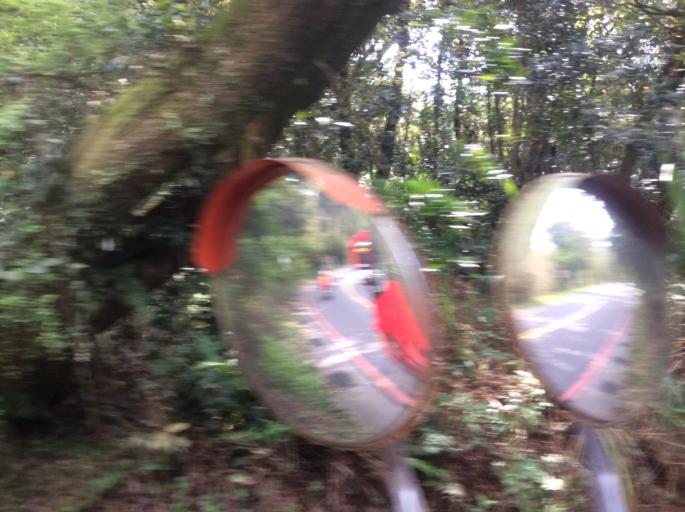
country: TW
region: Taipei
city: Taipei
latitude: 25.1614
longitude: 121.5443
